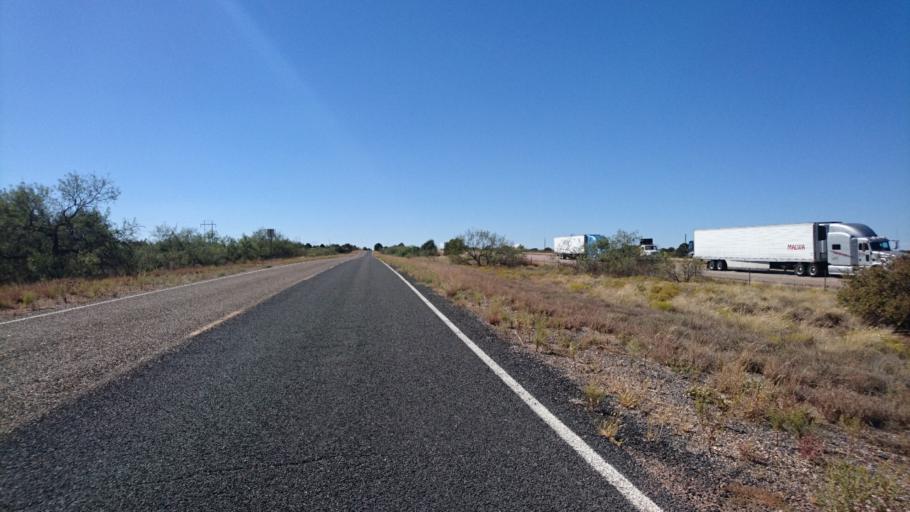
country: US
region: New Mexico
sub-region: Quay County
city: Tucumcari
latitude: 35.0693
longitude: -104.1659
